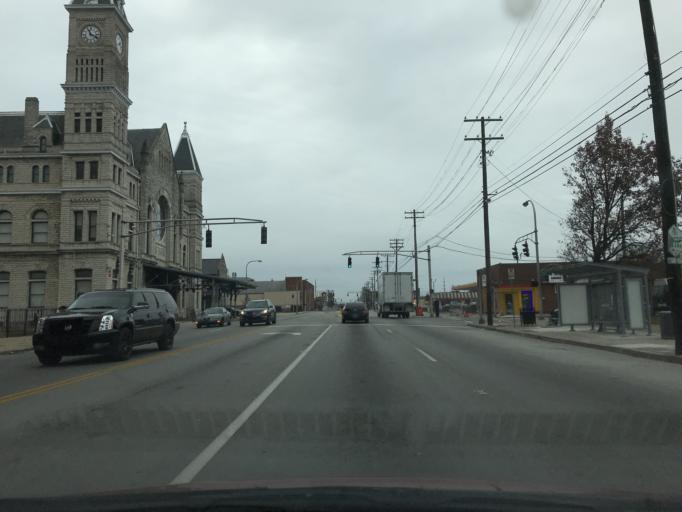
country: US
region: Kentucky
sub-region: Jefferson County
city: Louisville
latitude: 38.2471
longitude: -85.7678
